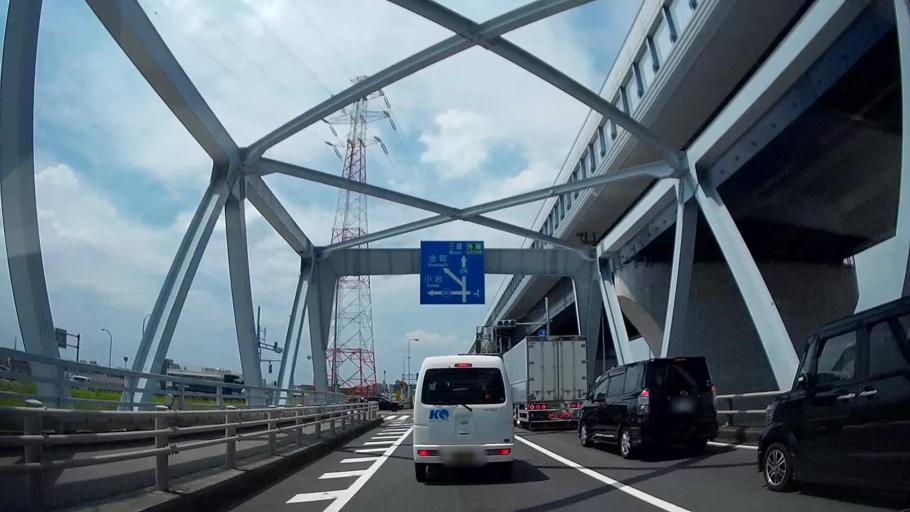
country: JP
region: Chiba
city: Matsudo
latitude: 35.7777
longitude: 139.8874
